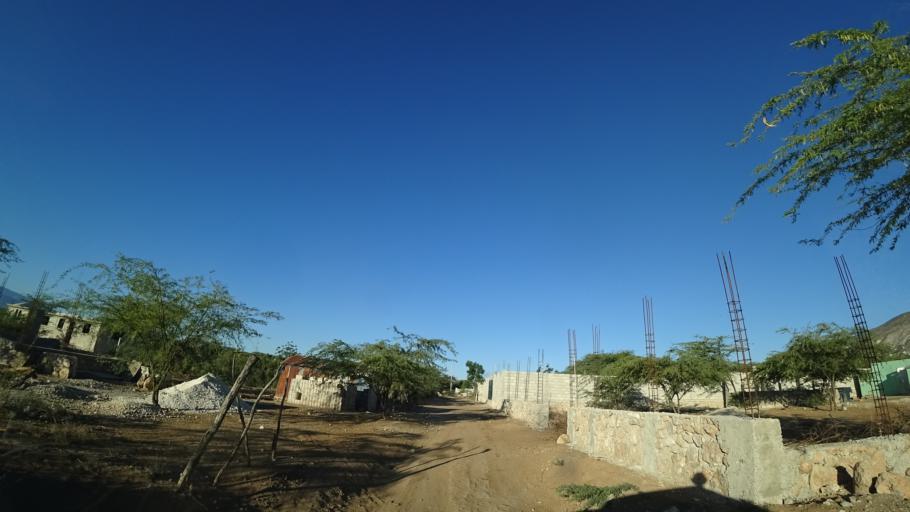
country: HT
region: Ouest
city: Croix des Bouquets
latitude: 18.6616
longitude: -72.2221
